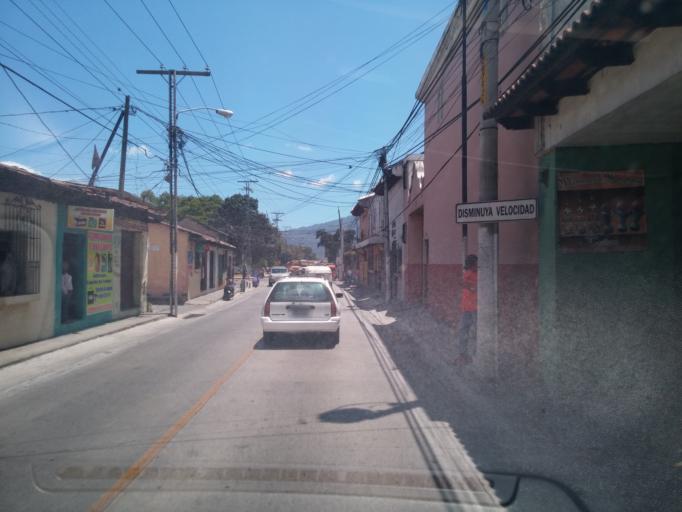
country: GT
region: Sacatepequez
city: Jocotenango
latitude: 14.5757
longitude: -90.7422
